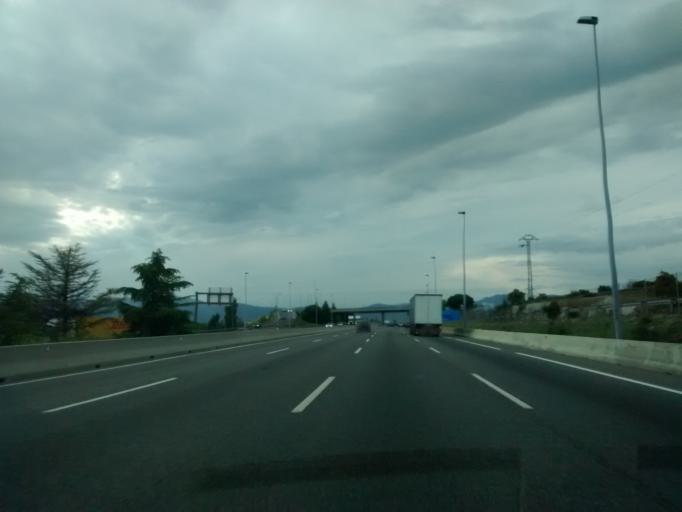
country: ES
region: Madrid
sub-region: Provincia de Madrid
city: Collado-Villalba
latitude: 40.6206
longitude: -3.9867
